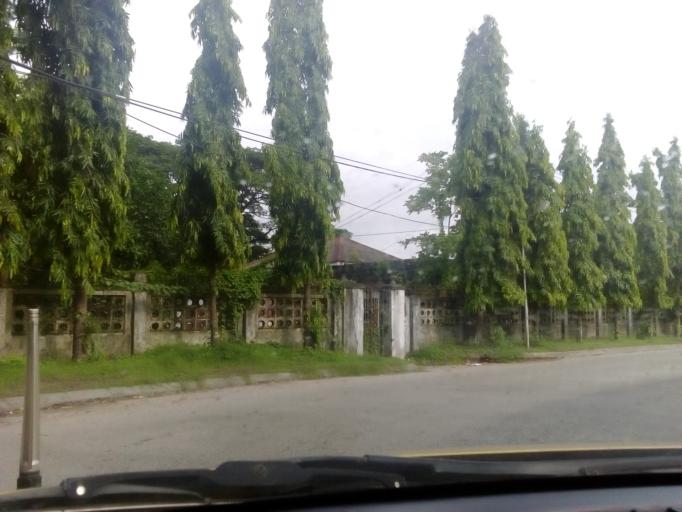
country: MM
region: Yangon
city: Yangon
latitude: 16.8475
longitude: 96.1531
